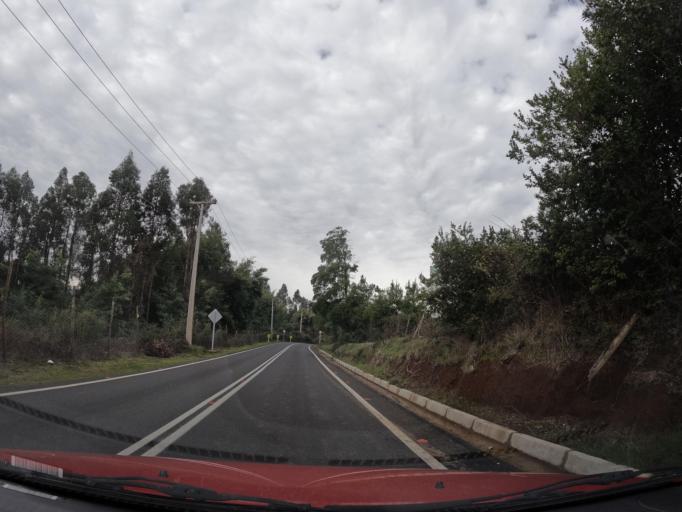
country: CL
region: Maule
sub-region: Provincia de Linares
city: Linares
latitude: -35.9153
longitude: -71.4688
